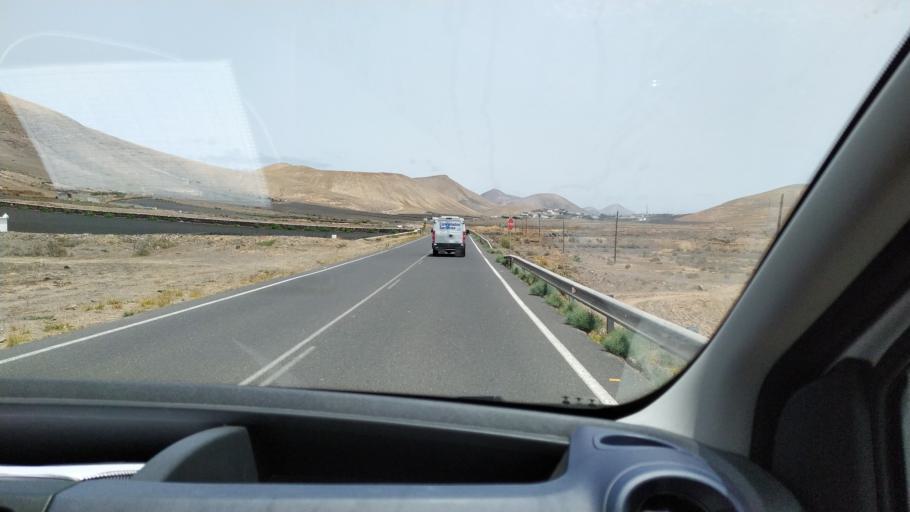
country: ES
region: Canary Islands
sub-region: Provincia de Las Palmas
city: Yaiza
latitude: 28.9223
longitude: -13.7673
